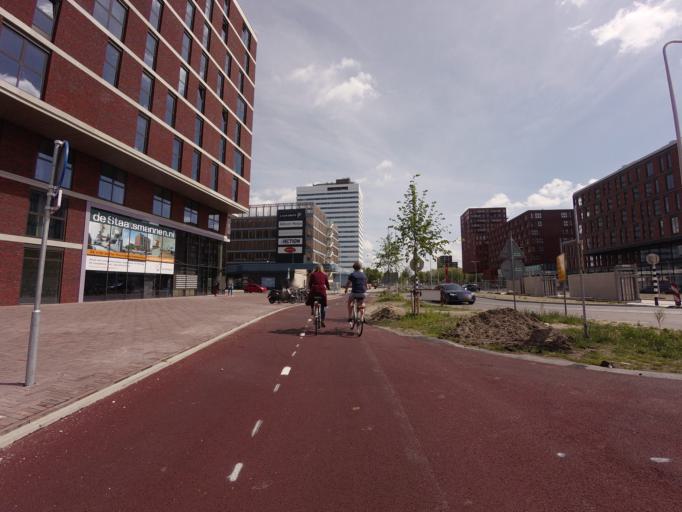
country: NL
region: Utrecht
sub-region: Gemeente Utrecht
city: Utrecht
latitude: 52.0730
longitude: 5.0933
